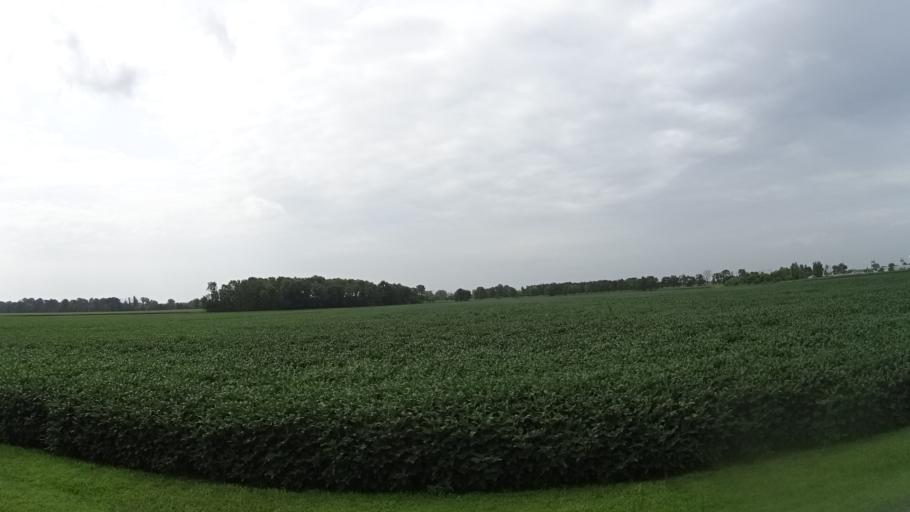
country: US
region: Indiana
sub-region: Madison County
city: Ingalls
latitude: 40.0024
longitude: -85.8362
